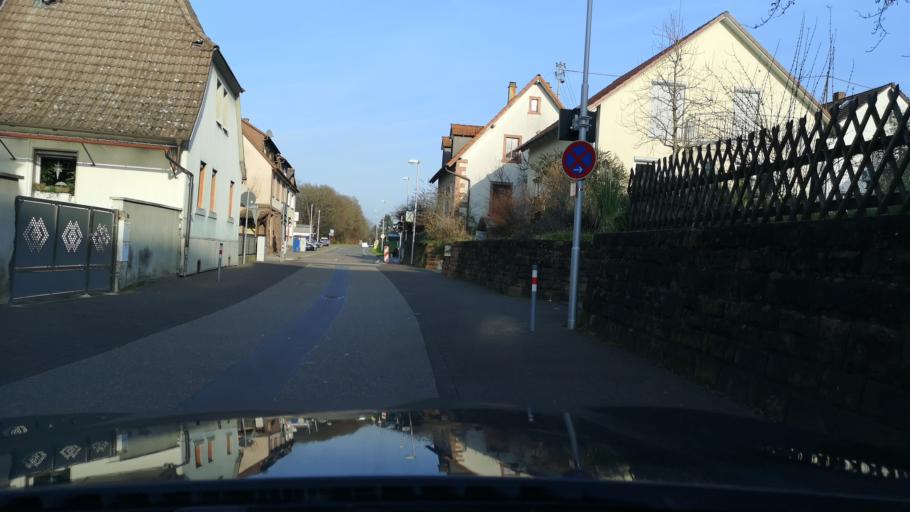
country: DE
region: Baden-Wuerttemberg
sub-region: Karlsruhe Region
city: Ettlingen
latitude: 48.9751
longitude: 8.4547
